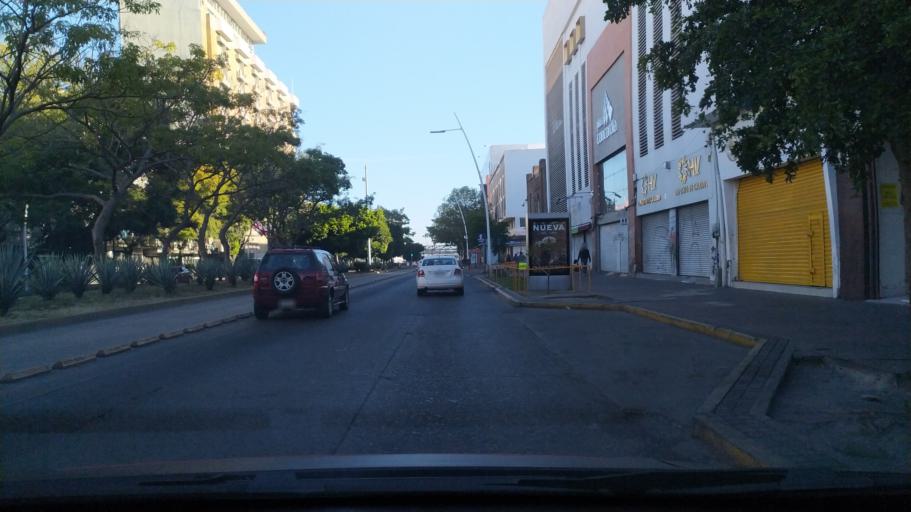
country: MX
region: Jalisco
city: Guadalajara
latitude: 20.6732
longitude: -103.3428
